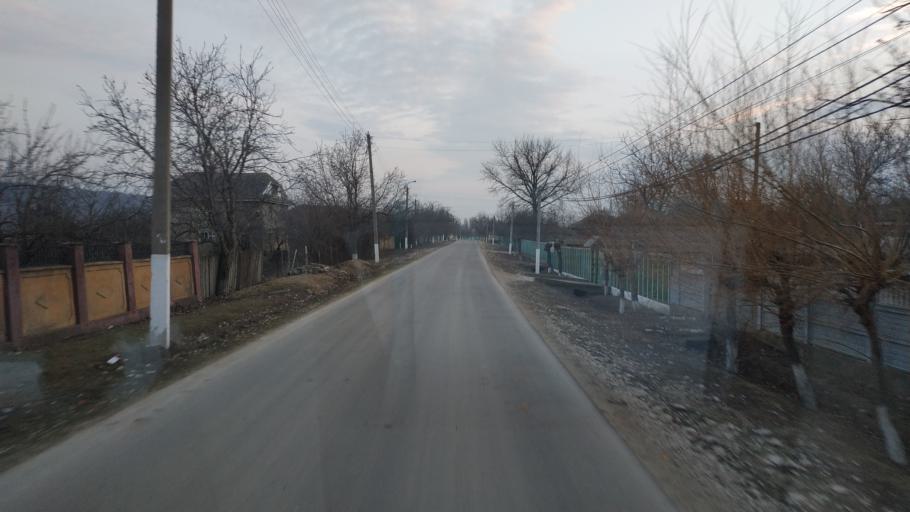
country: RO
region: Vaslui
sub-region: Comuna Stanilesti
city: Stanilesti
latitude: 46.6578
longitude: 28.3062
